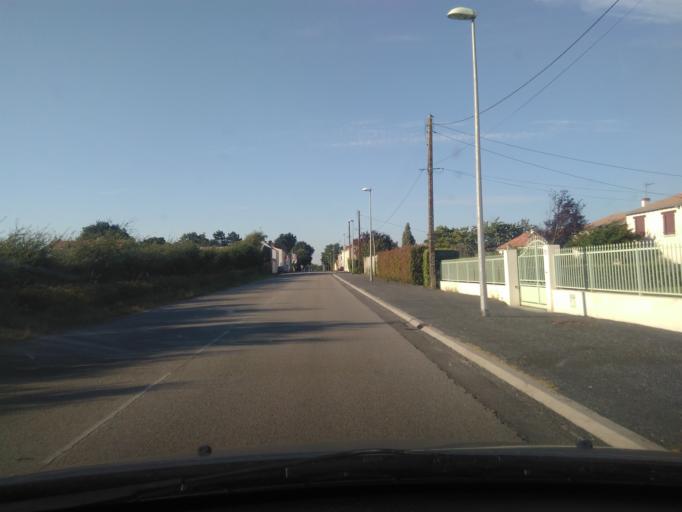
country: FR
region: Pays de la Loire
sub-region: Departement de la Vendee
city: Mouilleron-le-Captif
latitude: 46.7329
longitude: -1.4301
